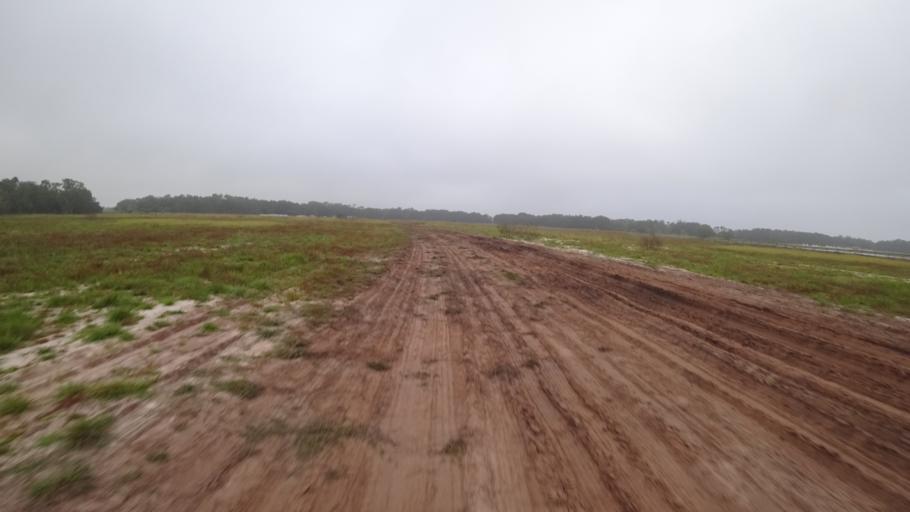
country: US
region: Florida
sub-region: Sarasota County
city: Lake Sarasota
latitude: 27.2933
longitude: -82.2160
